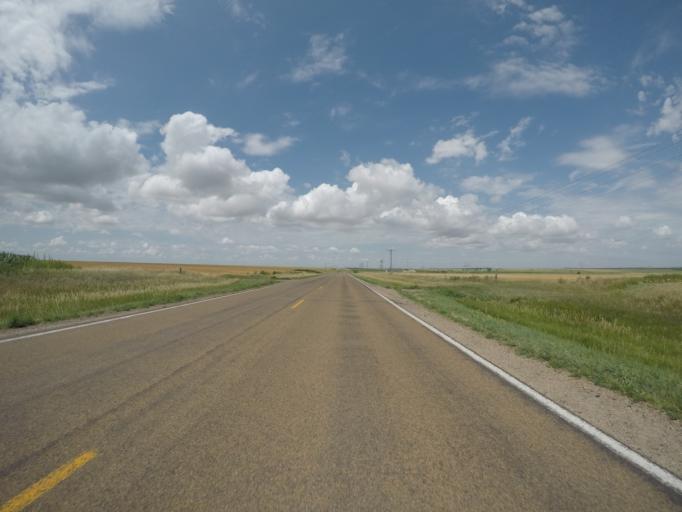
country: US
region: Kansas
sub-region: Rawlins County
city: Atwood
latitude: 39.8786
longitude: -101.0467
